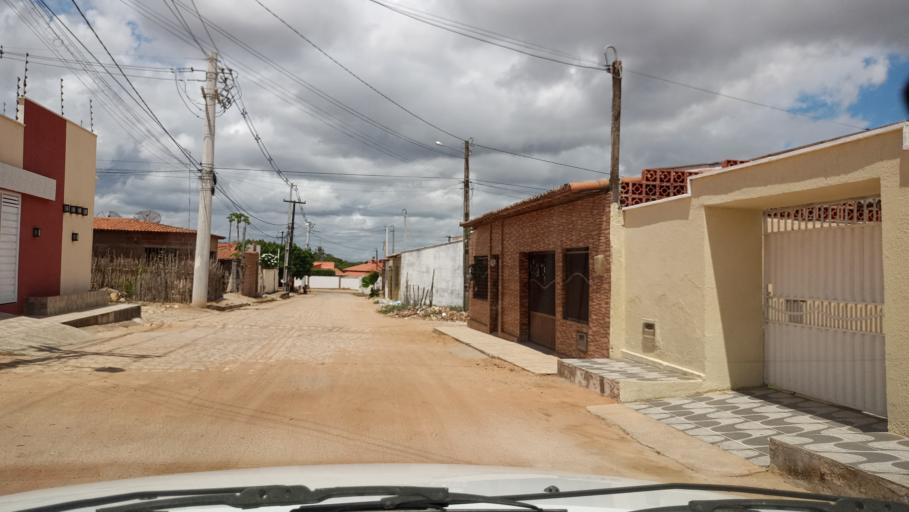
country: BR
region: Rio Grande do Norte
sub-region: Joao Camara
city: Joao Camara
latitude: -5.5276
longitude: -35.8101
